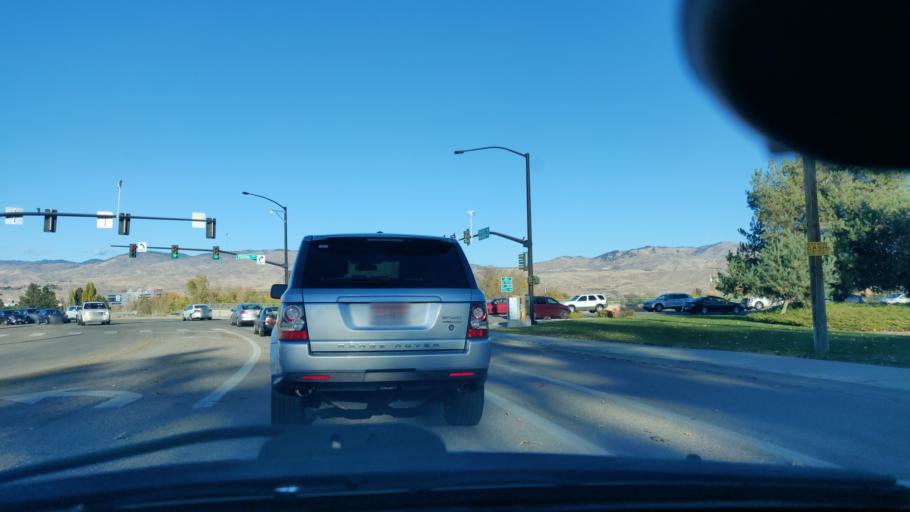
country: US
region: Idaho
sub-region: Ada County
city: Boise
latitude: 43.5936
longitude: -116.2068
